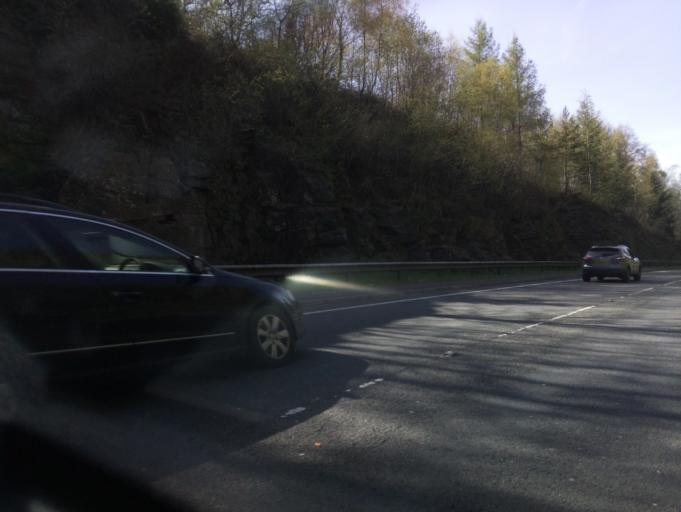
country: GB
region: Wales
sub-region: Rhondda Cynon Taf
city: Mountain Ash
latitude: 51.6671
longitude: -3.3550
